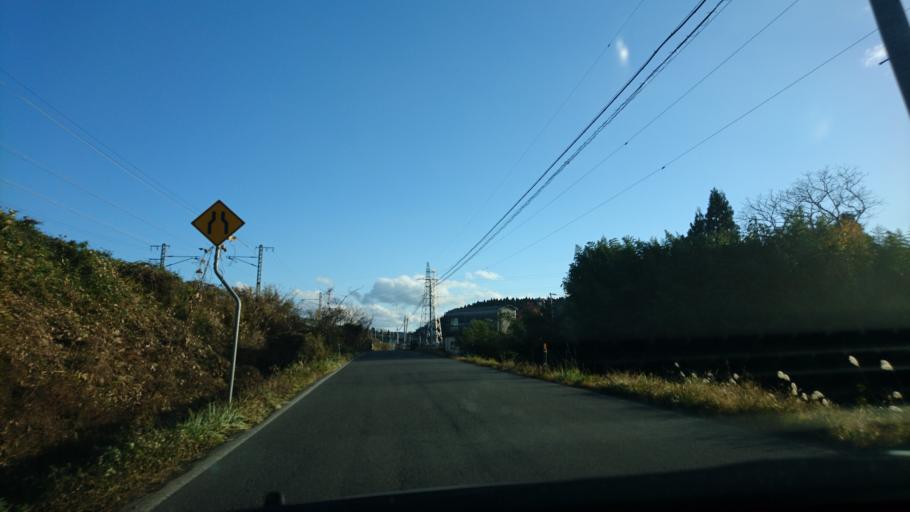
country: JP
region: Iwate
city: Mizusawa
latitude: 39.0291
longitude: 141.1277
